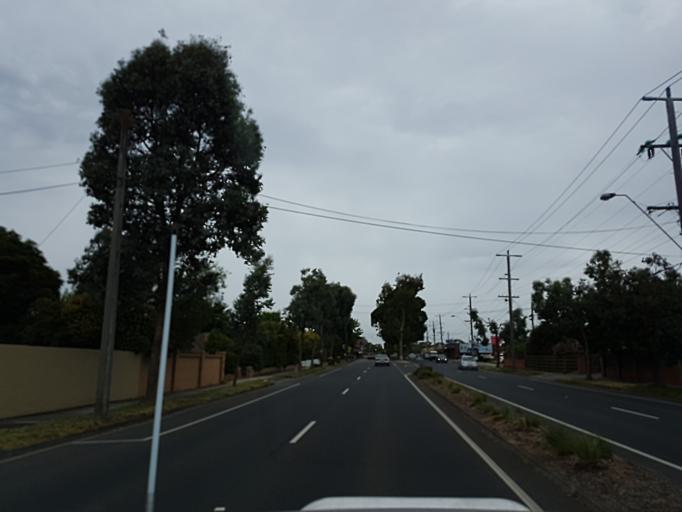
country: AU
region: Victoria
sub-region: Whitehorse
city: Blackburn South
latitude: -37.8313
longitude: 145.1445
